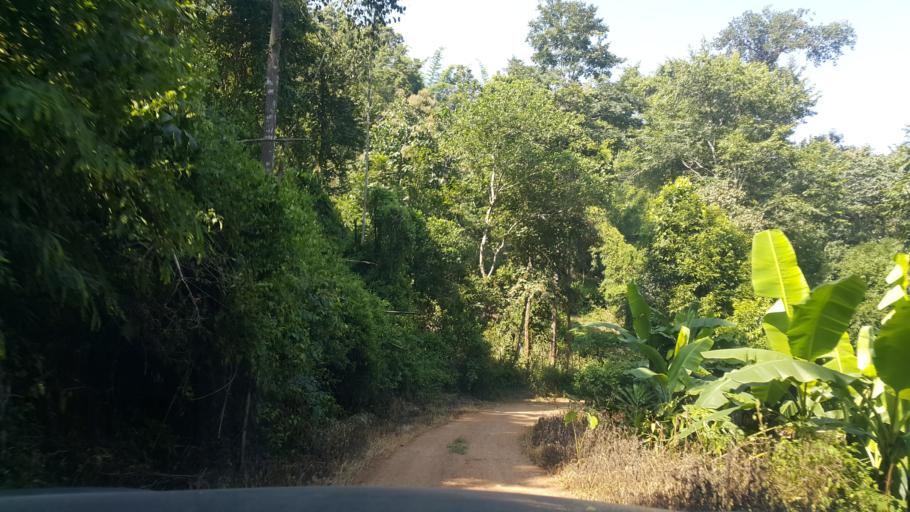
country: TH
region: Chiang Mai
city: Samoeng
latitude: 18.9414
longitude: 98.6193
